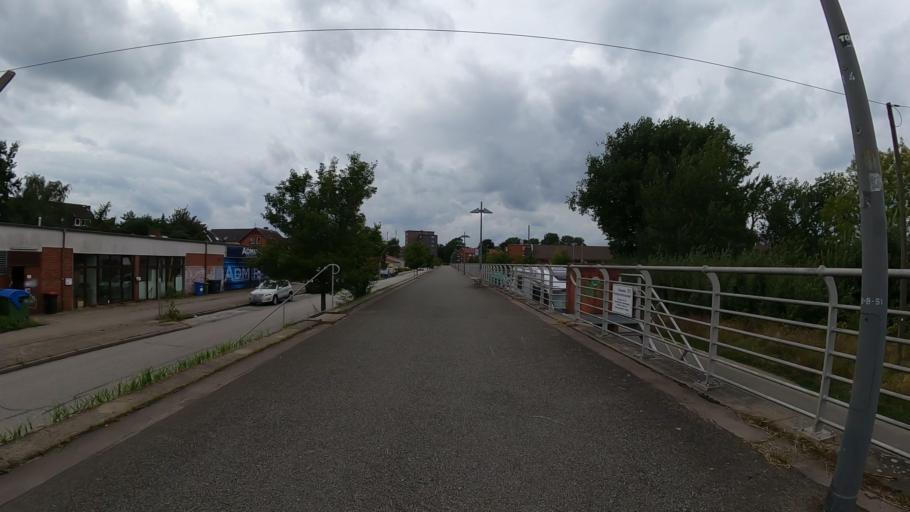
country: DE
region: Hamburg
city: Altona
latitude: 53.5321
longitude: 9.8827
